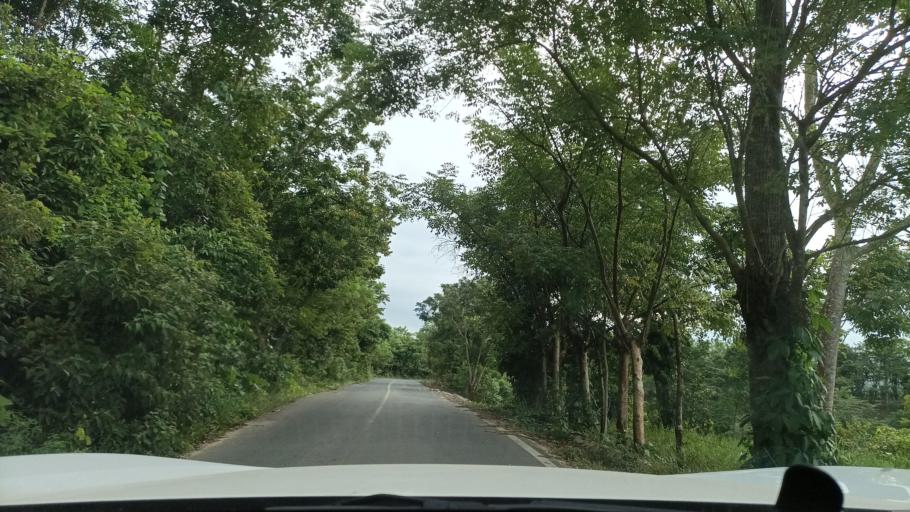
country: MX
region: Veracruz
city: Hidalgotitlan
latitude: 17.6901
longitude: -94.4534
